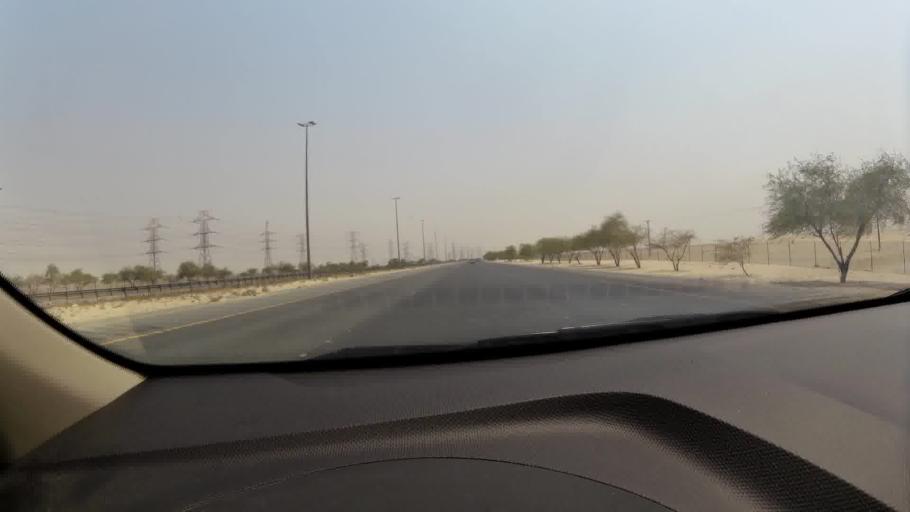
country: KW
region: Al Asimah
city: Ar Rabiyah
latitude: 29.2111
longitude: 47.8842
